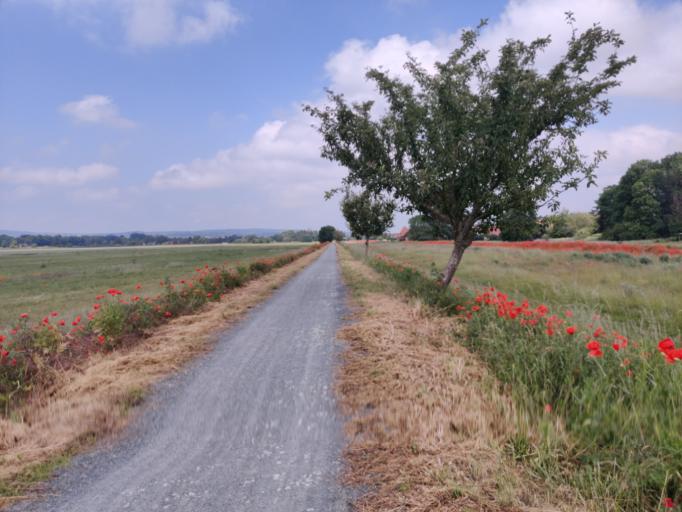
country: DE
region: Lower Saxony
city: Bad Salzdetfurth
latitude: 52.1085
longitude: 9.9980
